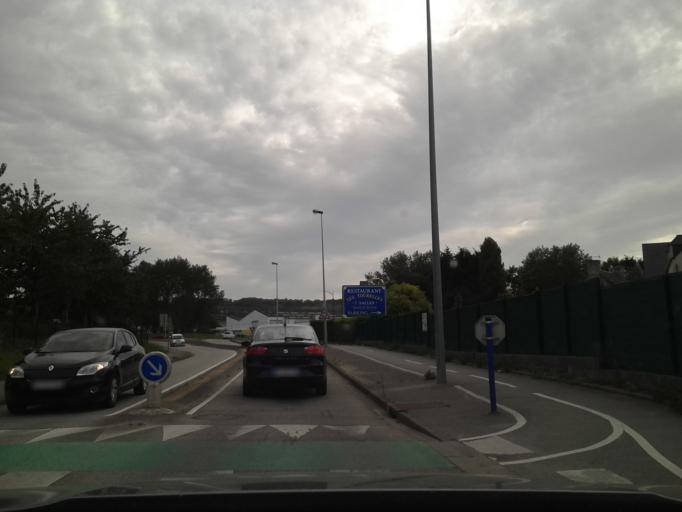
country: FR
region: Lower Normandy
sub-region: Departement de la Manche
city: Tourlaville
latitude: 49.6373
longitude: -1.5751
